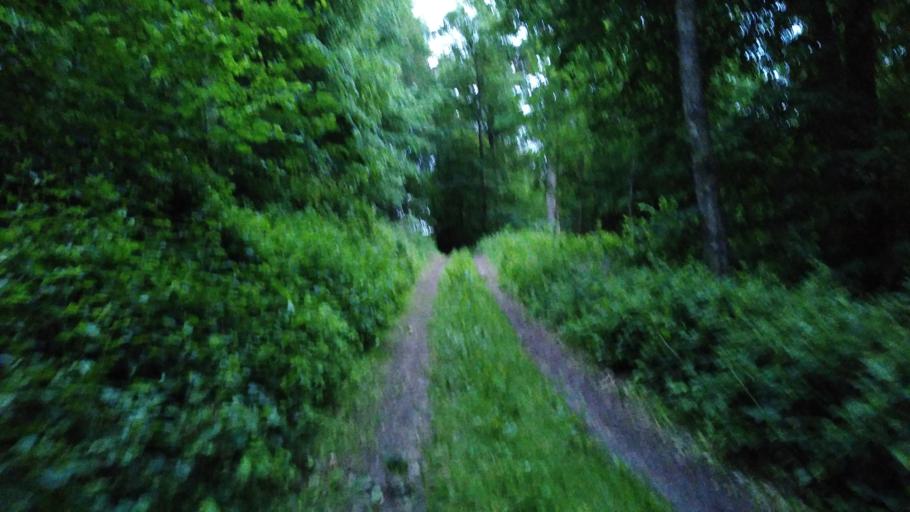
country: DE
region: Schleswig-Holstein
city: Kabelhorst
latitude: 54.2283
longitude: 10.9135
